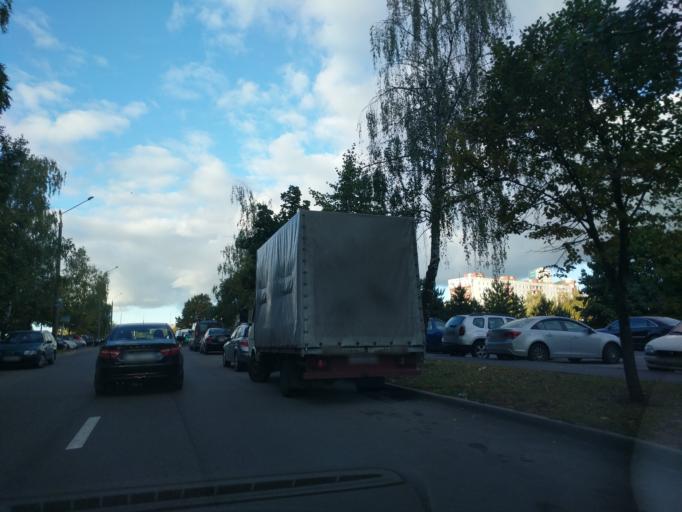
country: BY
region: Minsk
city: Malinovka
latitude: 53.8574
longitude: 27.4695
